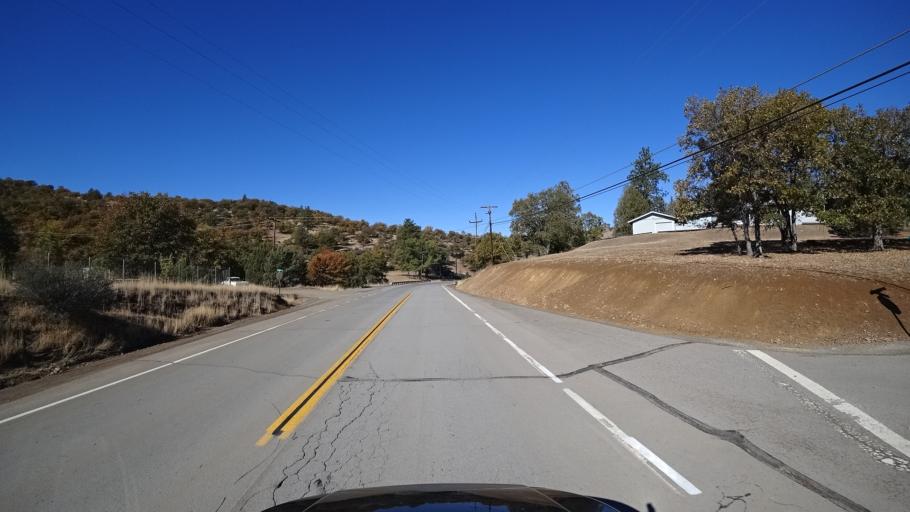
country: US
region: California
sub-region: Siskiyou County
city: Montague
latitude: 41.8945
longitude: -122.5049
